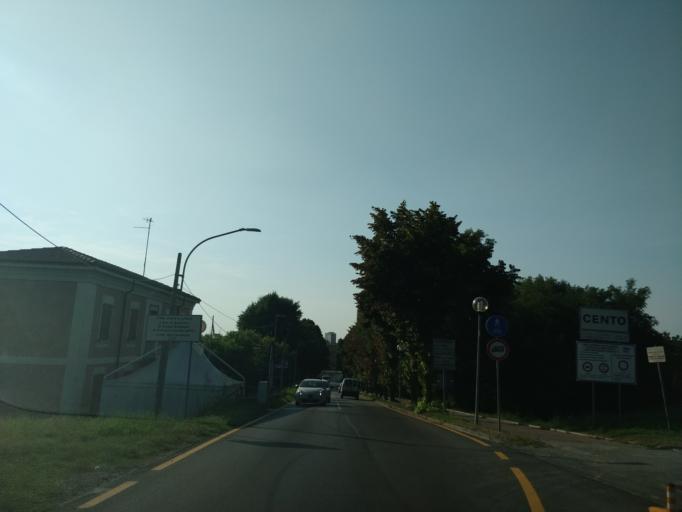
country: IT
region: Emilia-Romagna
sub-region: Provincia di Ferrara
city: Cento
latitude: 44.7215
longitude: 11.2953
